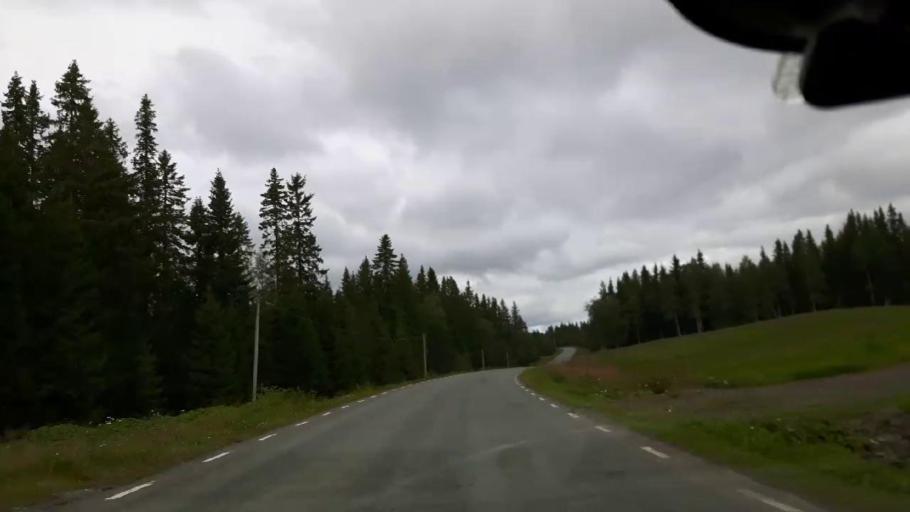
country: SE
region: Jaemtland
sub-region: Krokoms Kommun
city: Valla
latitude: 63.5144
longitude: 13.8780
